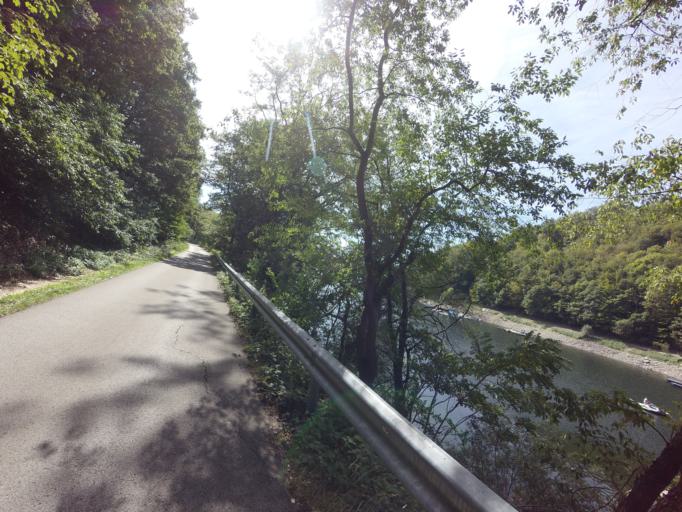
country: DE
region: North Rhine-Westphalia
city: Heimbach
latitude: 50.6354
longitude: 6.3918
